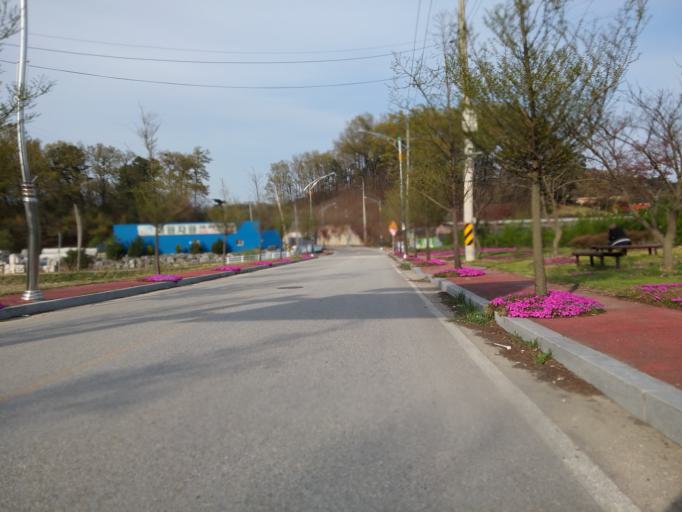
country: KR
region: Chungcheongbuk-do
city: Okcheon
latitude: 36.2715
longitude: 127.5875
